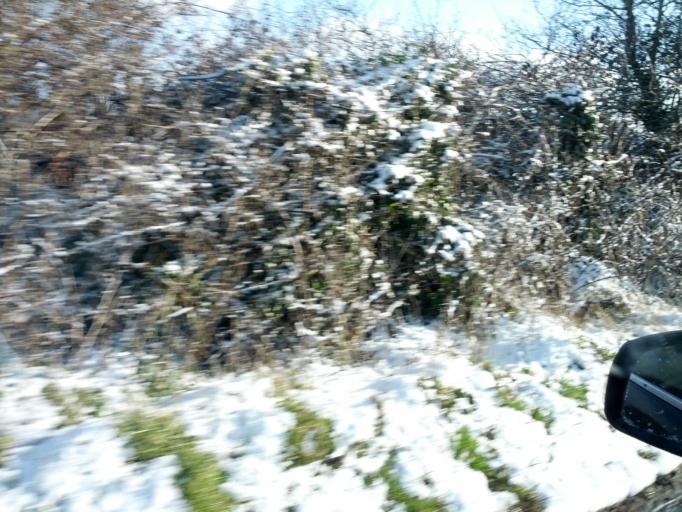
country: IE
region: Connaught
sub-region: County Galway
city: Gort
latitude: 53.1788
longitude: -8.7847
